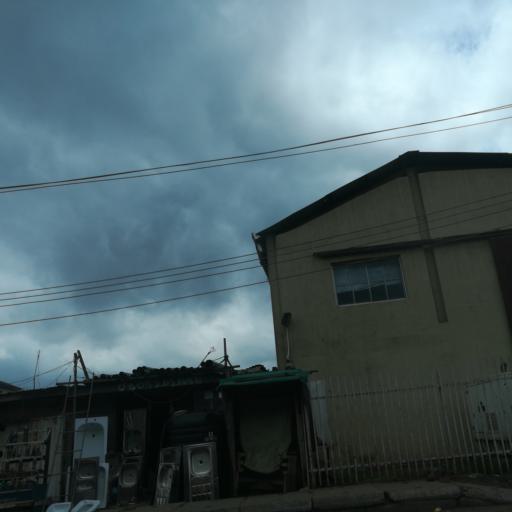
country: NG
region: Lagos
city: Mushin
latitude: 6.5315
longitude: 3.3395
